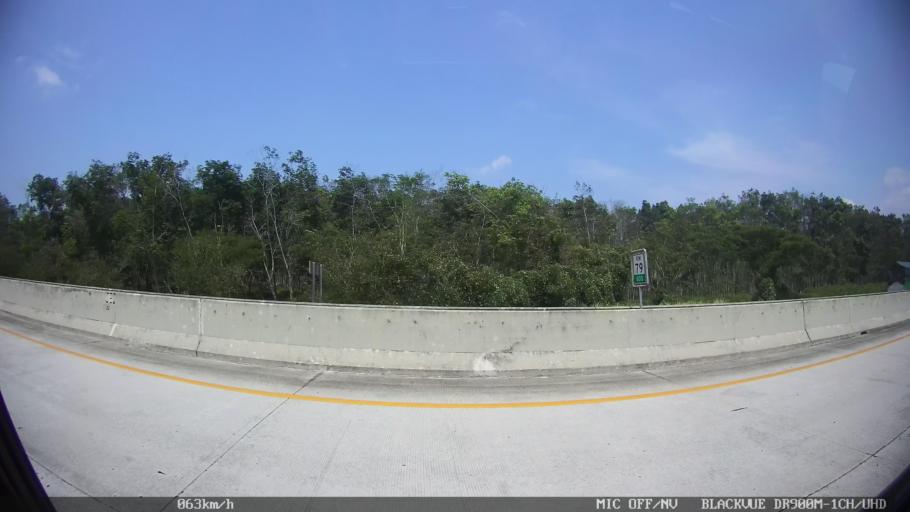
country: ID
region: Lampung
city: Kedaton
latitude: -5.3586
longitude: 105.3247
